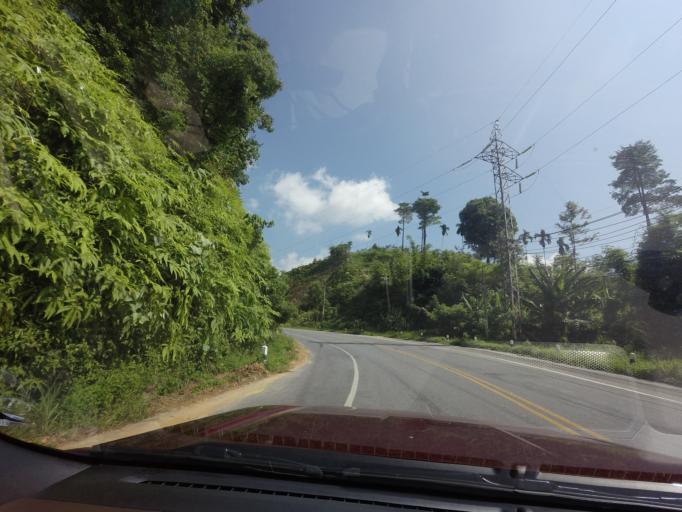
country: TH
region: Yala
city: Betong
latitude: 5.8594
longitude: 101.1186
